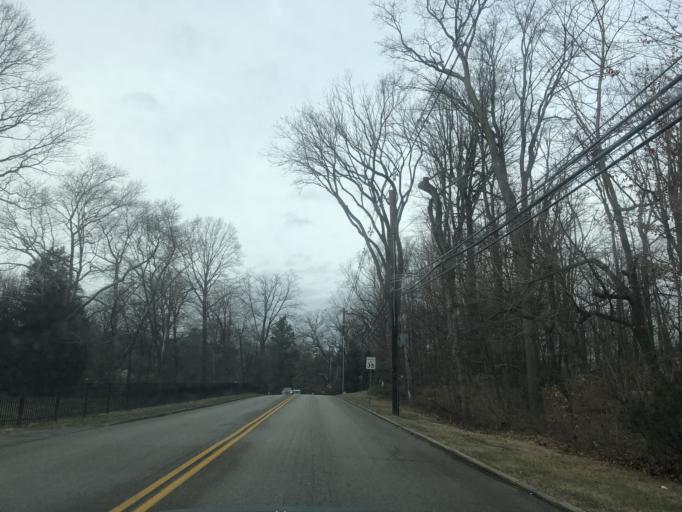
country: US
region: Pennsylvania
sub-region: Delaware County
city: Radnor
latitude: 40.0448
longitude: -75.3350
